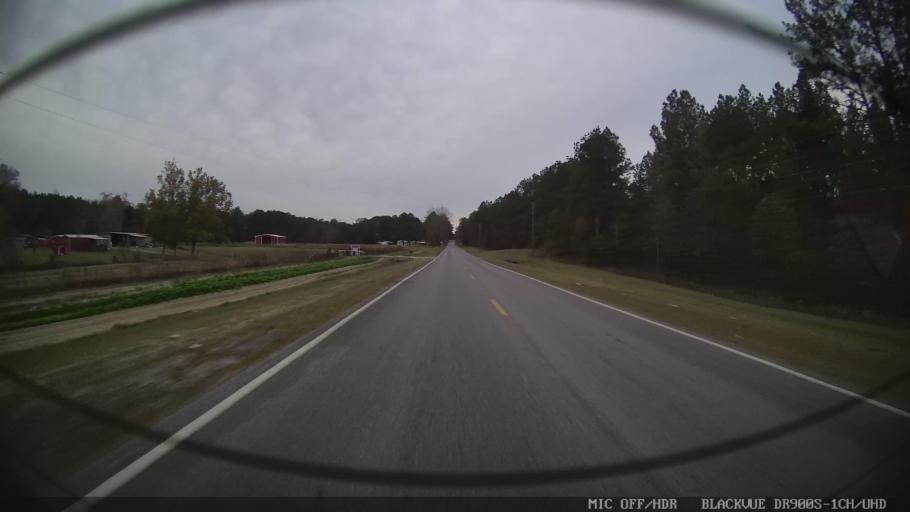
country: US
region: Mississippi
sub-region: Clarke County
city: Quitman
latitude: 32.0289
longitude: -88.8060
